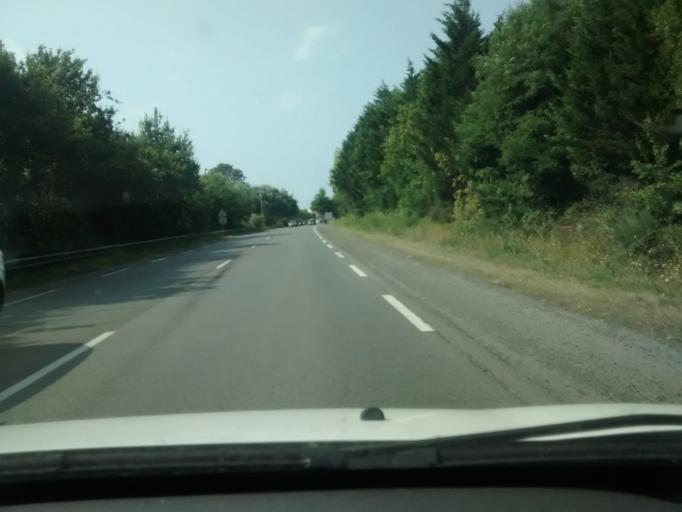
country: FR
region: Pays de la Loire
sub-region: Departement de la Loire-Atlantique
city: Pornichet
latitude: 47.2689
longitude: -2.3294
